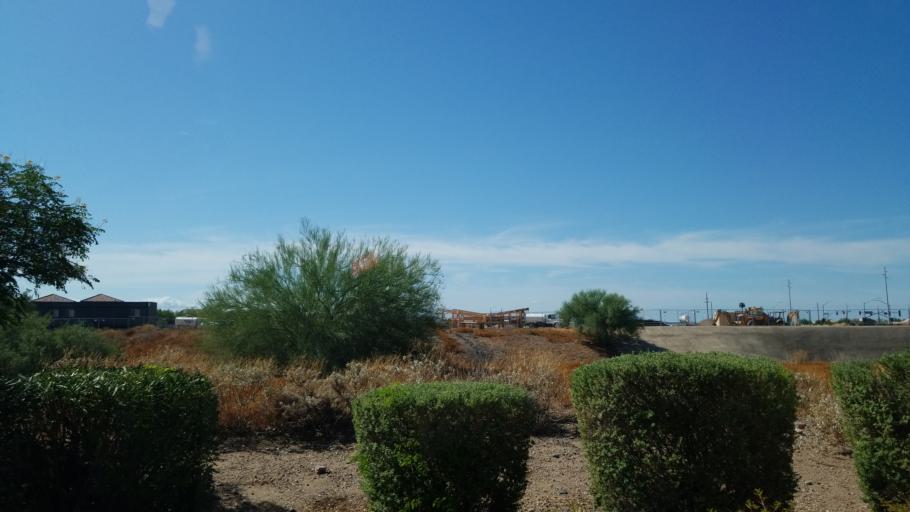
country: US
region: Arizona
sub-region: Maricopa County
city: Peoria
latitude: 33.6364
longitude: -112.2185
